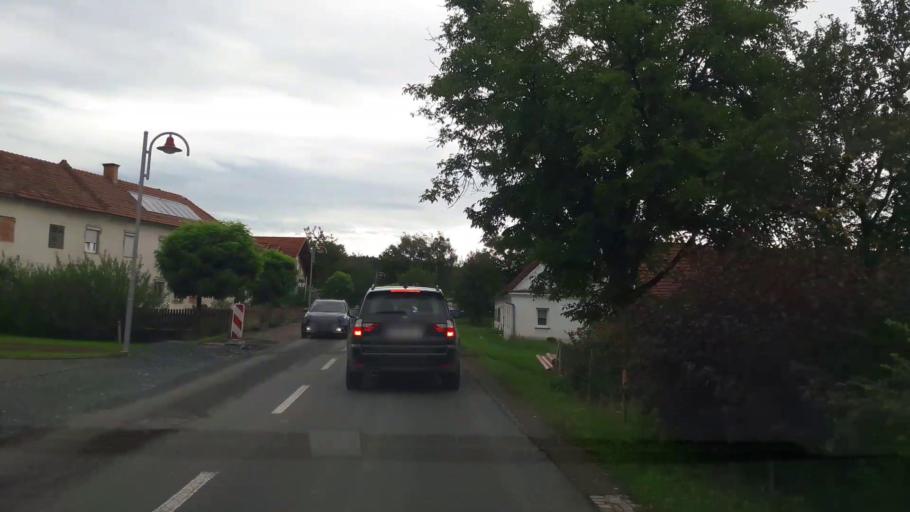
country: AT
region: Styria
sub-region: Politischer Bezirk Hartberg-Fuerstenfeld
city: Ebersdorf
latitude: 47.1982
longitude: 15.9629
